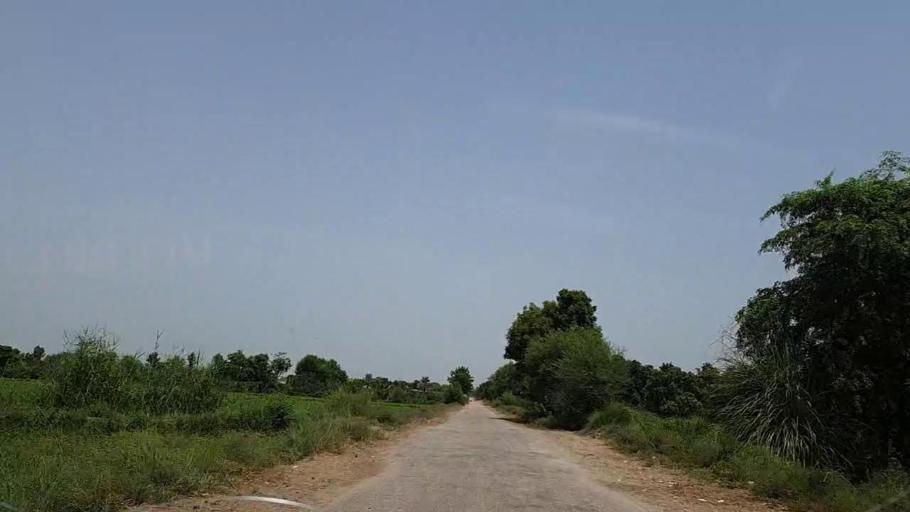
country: PK
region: Sindh
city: Tharu Shah
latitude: 26.9473
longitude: 68.0254
